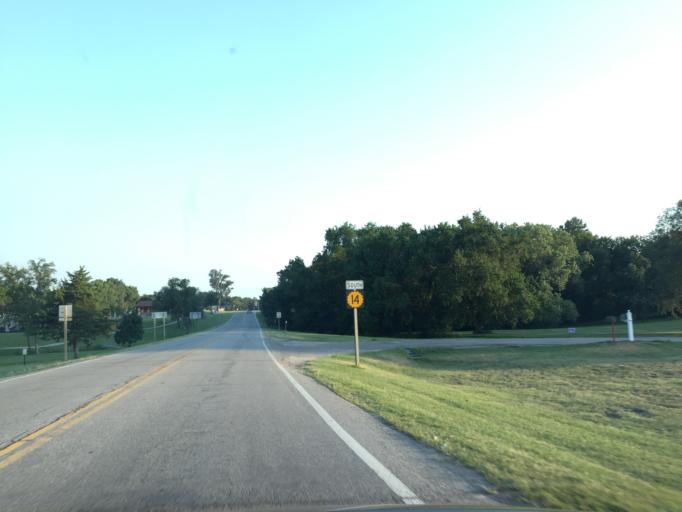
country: US
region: Kansas
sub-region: Ellsworth County
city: Ellsworth
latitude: 38.7399
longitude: -98.2252
